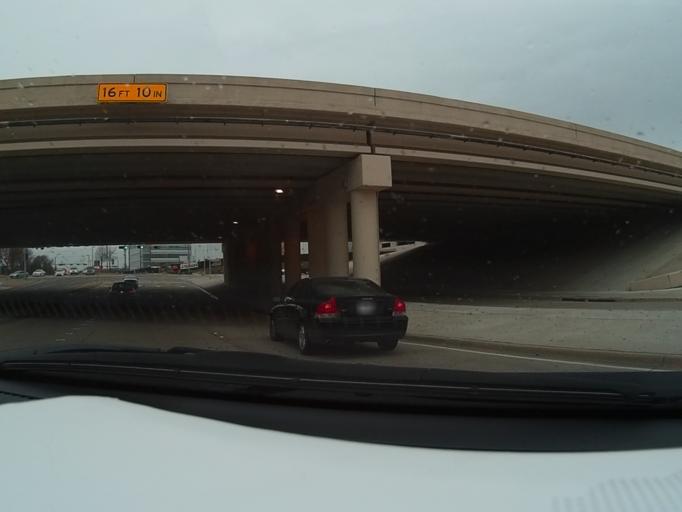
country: US
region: Texas
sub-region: Collin County
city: Allen
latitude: 33.0907
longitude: -96.6811
